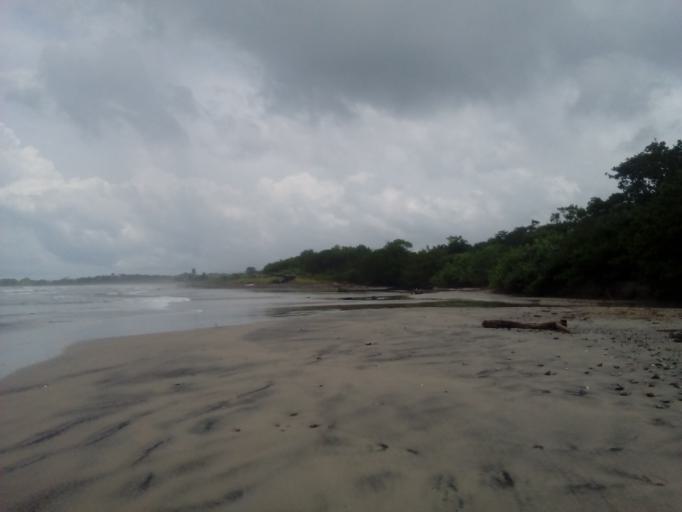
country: CR
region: Guanacaste
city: Samara
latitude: 9.9358
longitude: -85.6658
